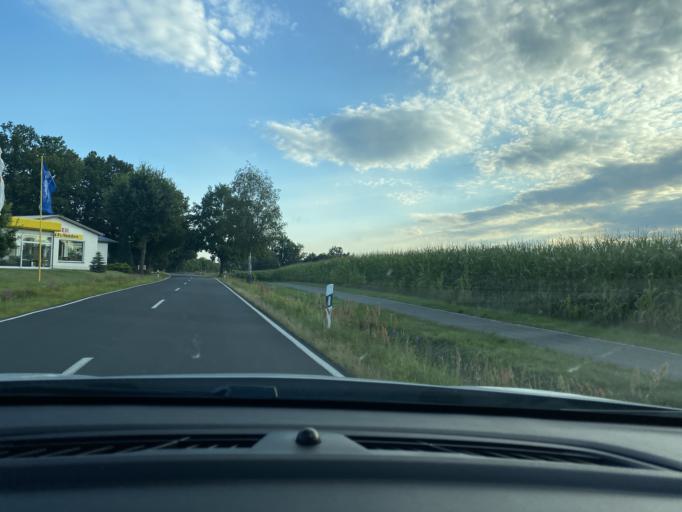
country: DE
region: Saxony
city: Horka
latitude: 51.2760
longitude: 14.8906
